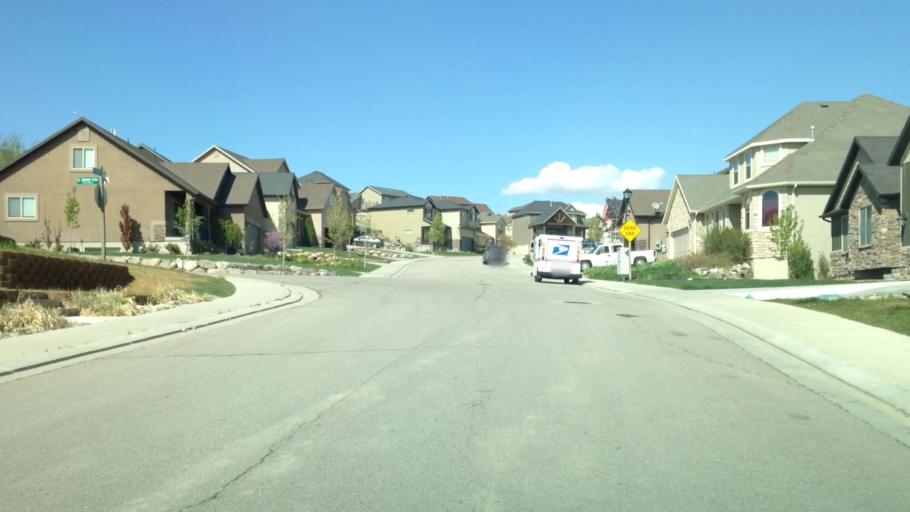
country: US
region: Utah
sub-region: Utah County
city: Saratoga Springs
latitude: 40.3767
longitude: -111.9676
